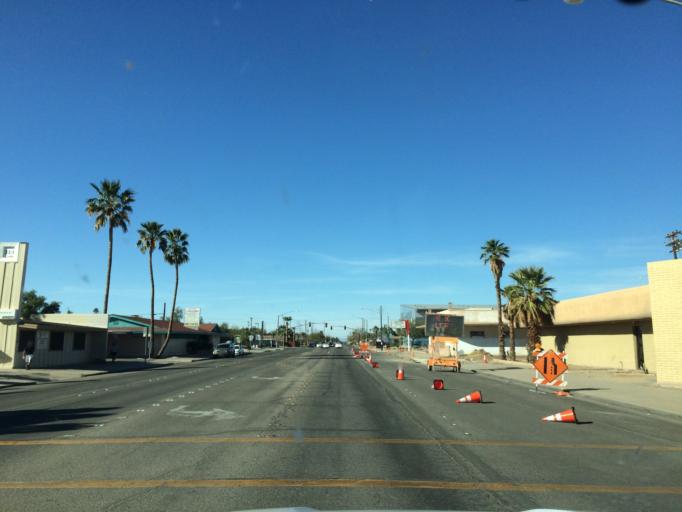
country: US
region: California
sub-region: Imperial County
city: El Centro
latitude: 32.7948
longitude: -115.5614
